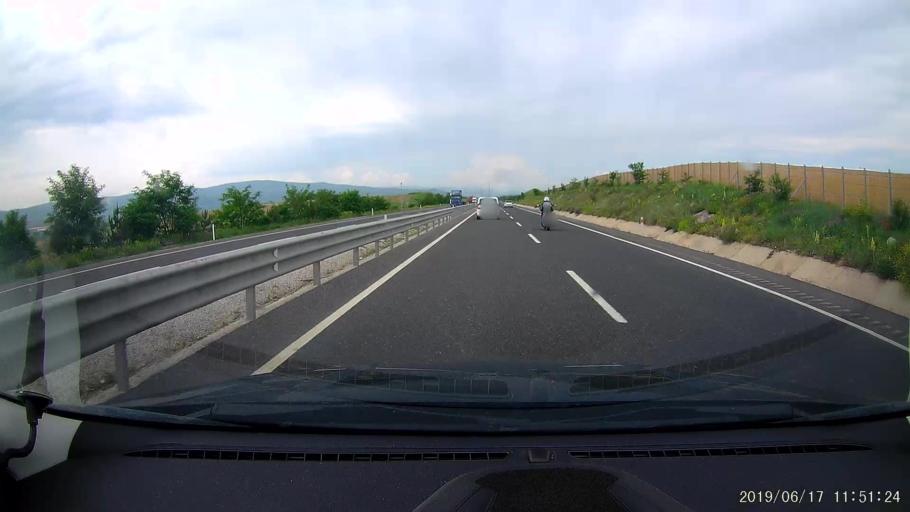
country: TR
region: Cankiri
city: Atkaracalar
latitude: 40.8185
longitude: 33.1074
